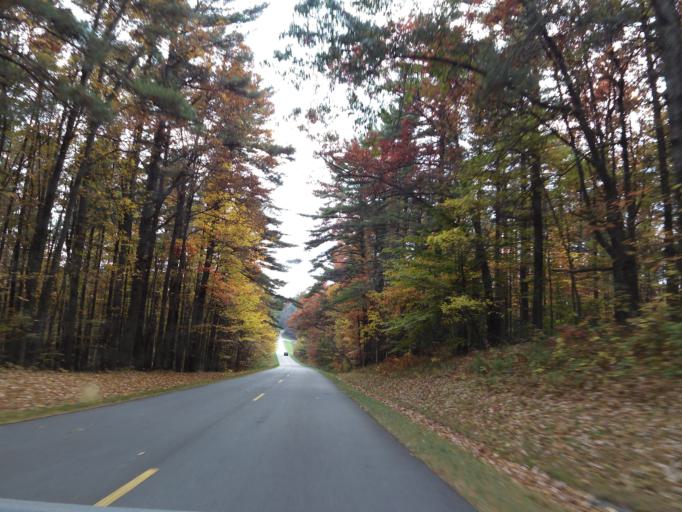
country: US
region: North Carolina
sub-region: Ashe County
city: Jefferson
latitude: 36.3709
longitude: -81.3460
